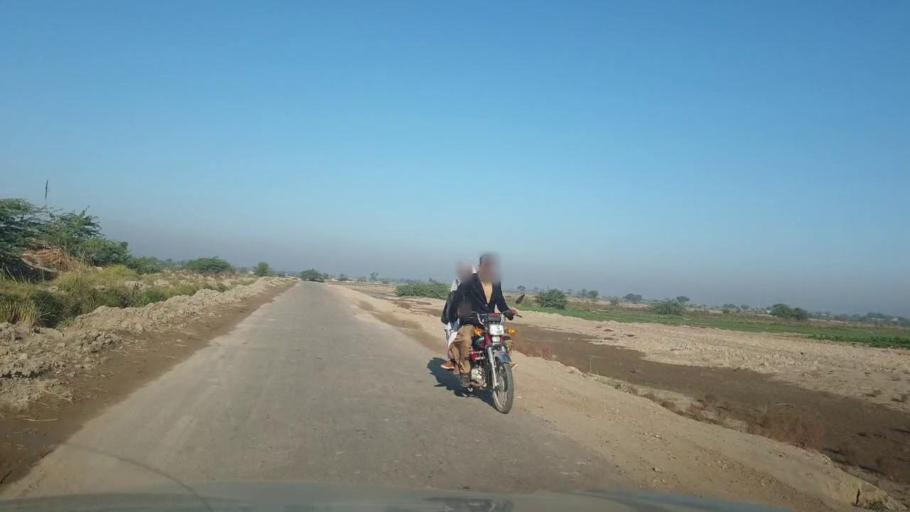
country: PK
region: Sindh
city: Bhan
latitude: 26.5517
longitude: 67.6975
